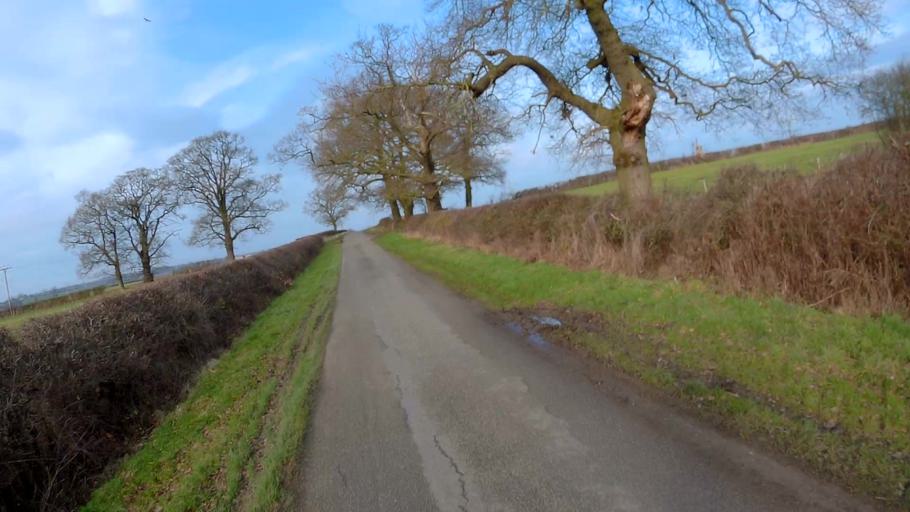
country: GB
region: England
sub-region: Lincolnshire
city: Bourne
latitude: 52.7654
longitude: -0.4209
